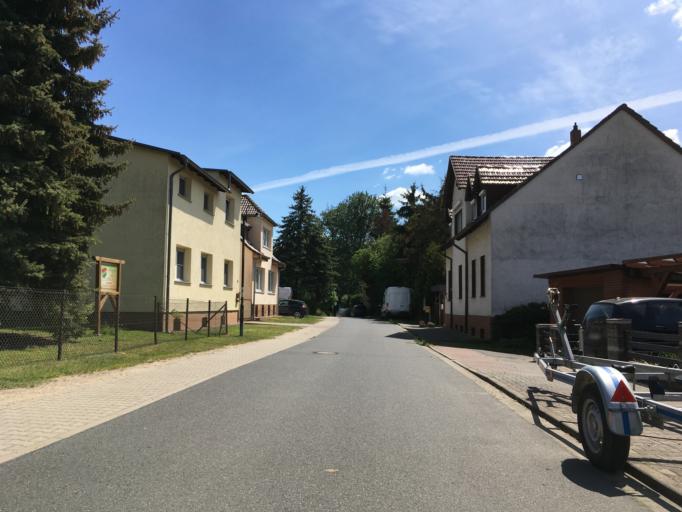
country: DE
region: Brandenburg
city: Niederfinow
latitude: 52.8406
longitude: 13.9020
